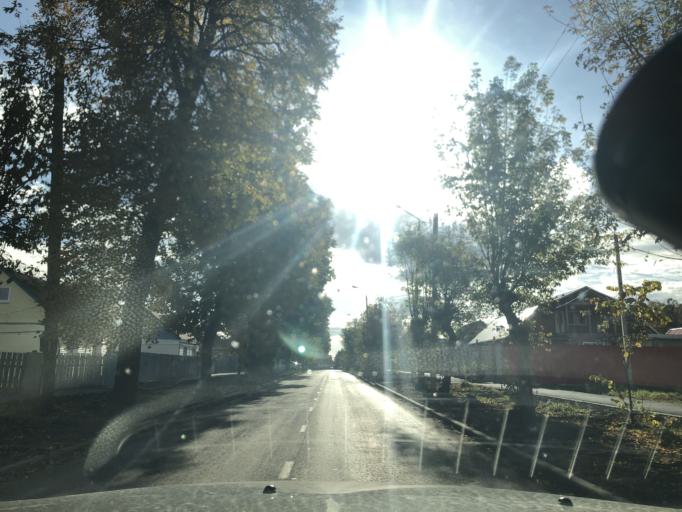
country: RU
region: Tula
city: Kireyevsk
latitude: 53.9364
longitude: 37.9313
